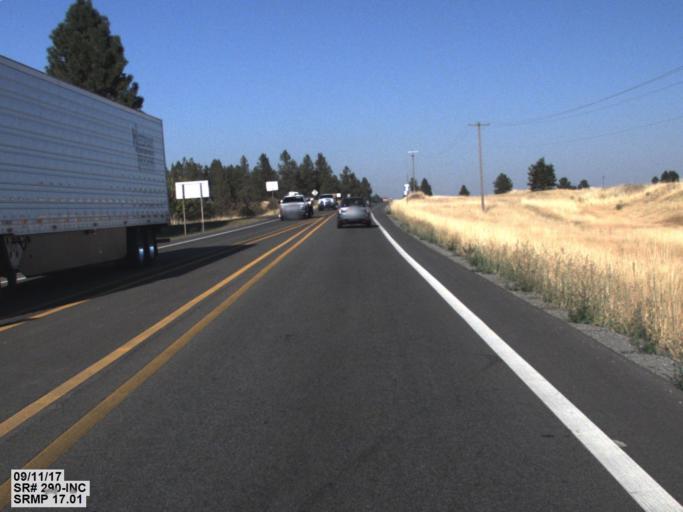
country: US
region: Washington
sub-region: Spokane County
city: Otis Orchards-East Farms
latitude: 47.7251
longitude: -117.0668
